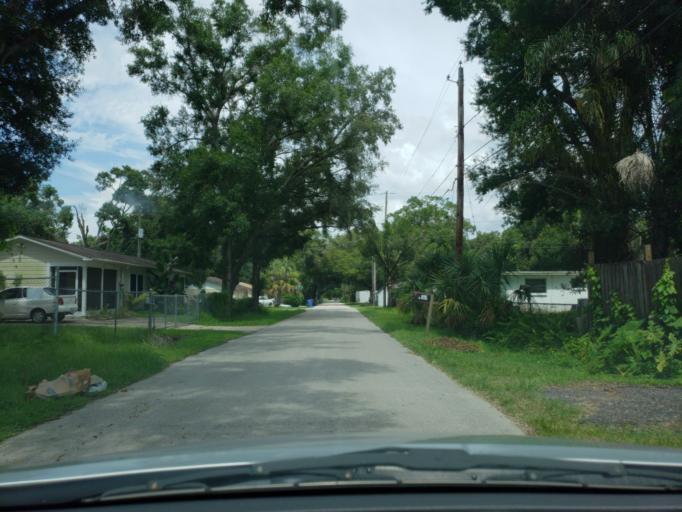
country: US
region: Florida
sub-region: Hillsborough County
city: East Lake-Orient Park
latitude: 27.9732
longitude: -82.3715
